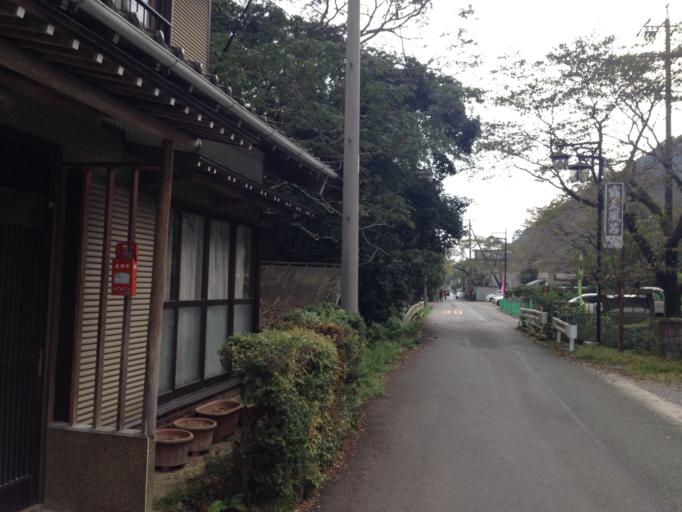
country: JP
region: Aichi
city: Shinshiro
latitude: 34.9734
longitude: 137.6147
